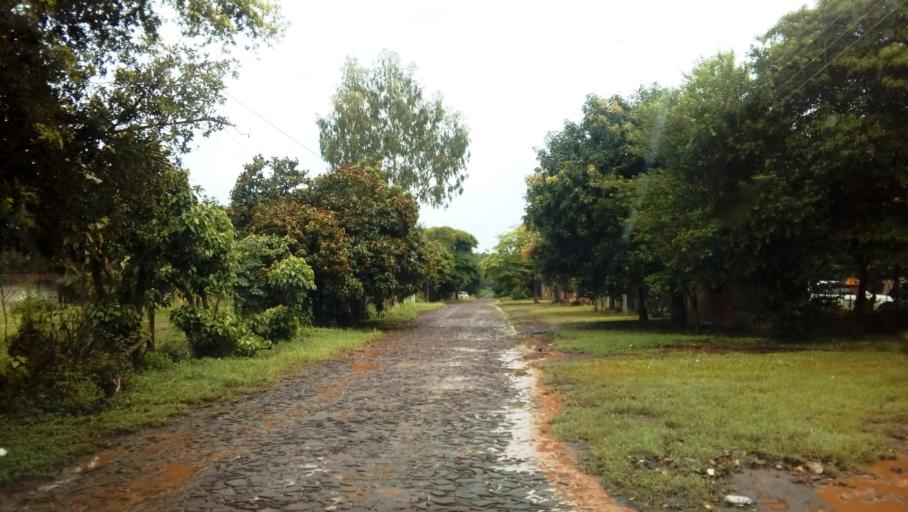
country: PY
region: Alto Parana
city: Ciudad del Este
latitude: -25.4201
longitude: -54.6393
